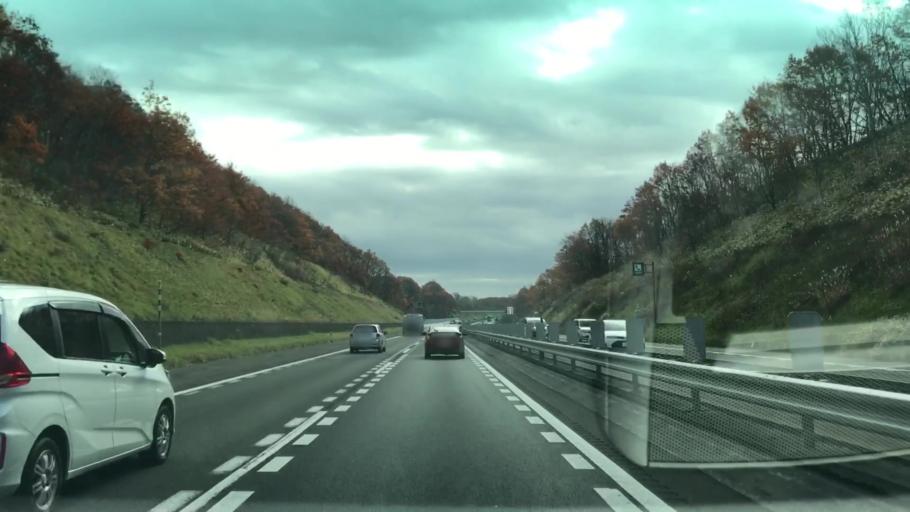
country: JP
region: Hokkaido
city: Kitahiroshima
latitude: 42.9262
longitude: 141.5380
